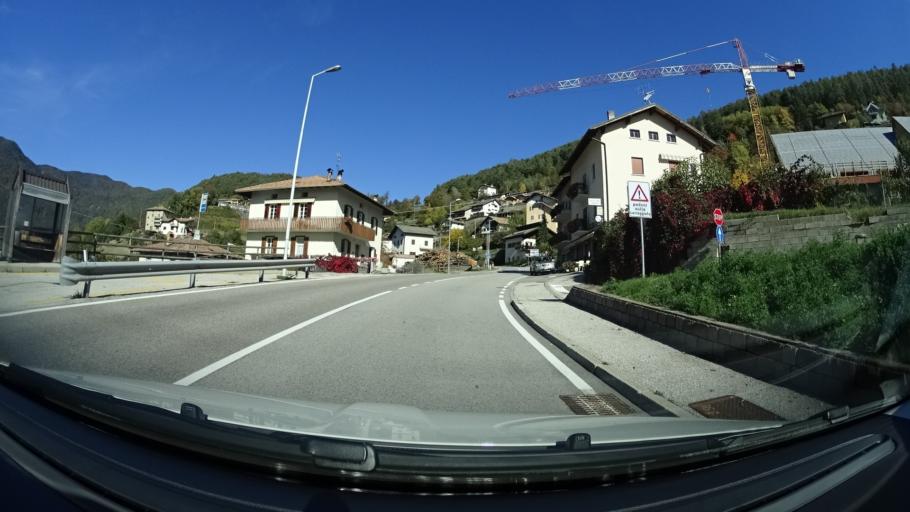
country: IT
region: Trentino-Alto Adige
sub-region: Provincia di Trento
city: Segonzano
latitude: 46.1914
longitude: 11.2590
